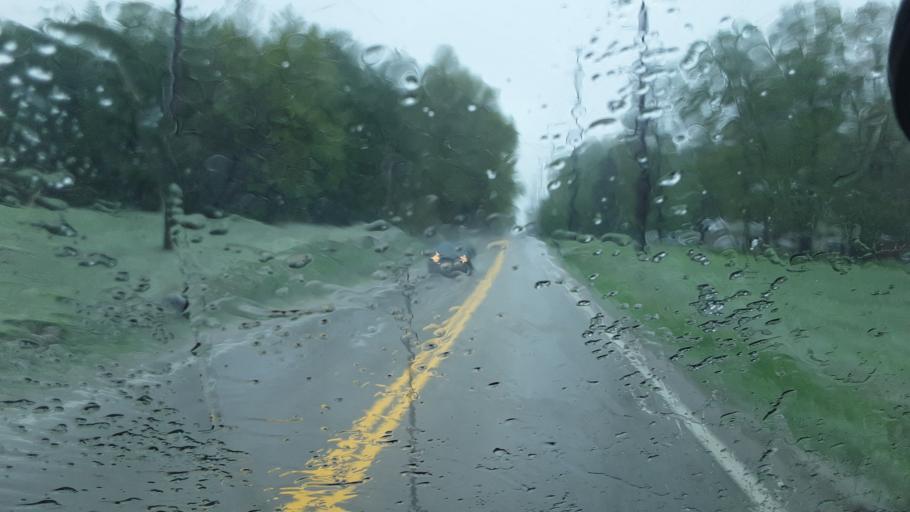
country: US
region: Ohio
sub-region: Portage County
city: Windham
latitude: 41.3093
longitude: -80.9956
